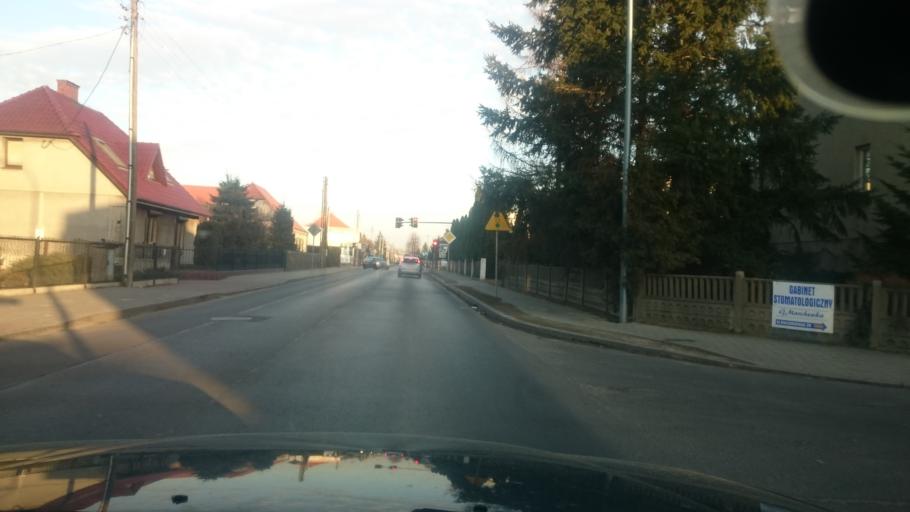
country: PL
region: Greater Poland Voivodeship
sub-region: Powiat ostrowski
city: Ostrow Wielkopolski
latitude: 51.6471
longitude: 17.8359
